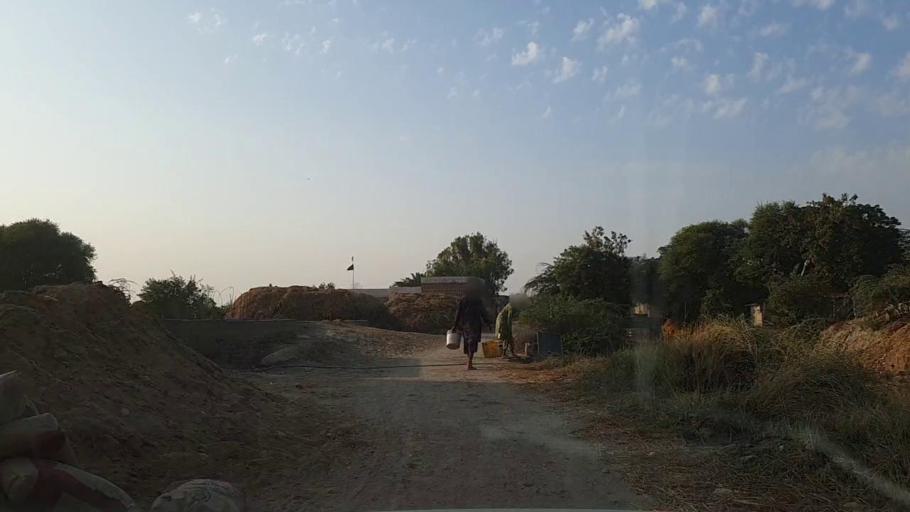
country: PK
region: Sindh
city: Daro Mehar
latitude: 24.7767
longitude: 68.1955
